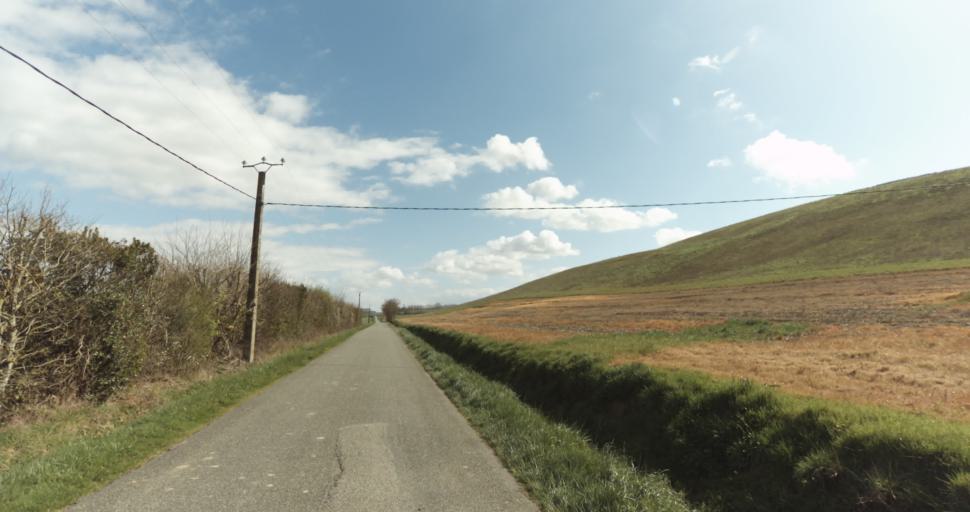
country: FR
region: Midi-Pyrenees
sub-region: Departement de la Haute-Garonne
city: Auterive
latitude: 43.3705
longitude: 1.5163
